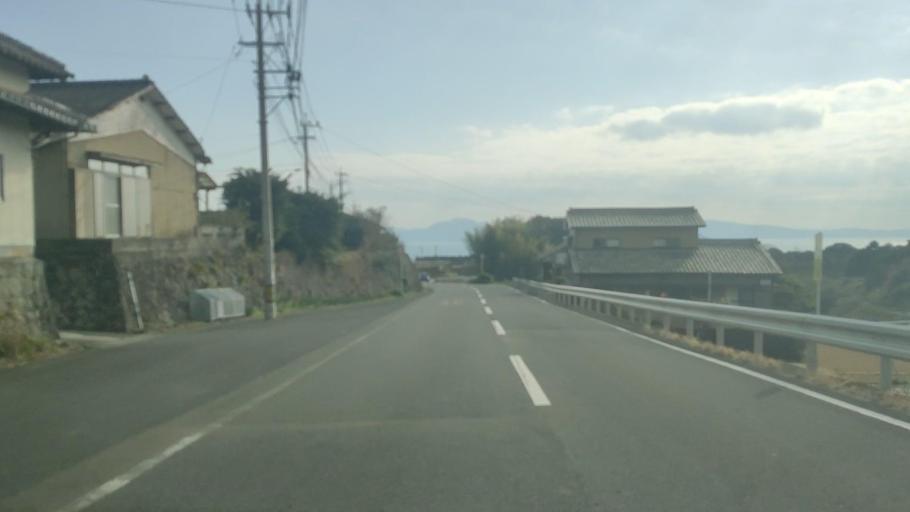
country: JP
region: Nagasaki
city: Shimabara
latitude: 32.6665
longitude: 130.2864
